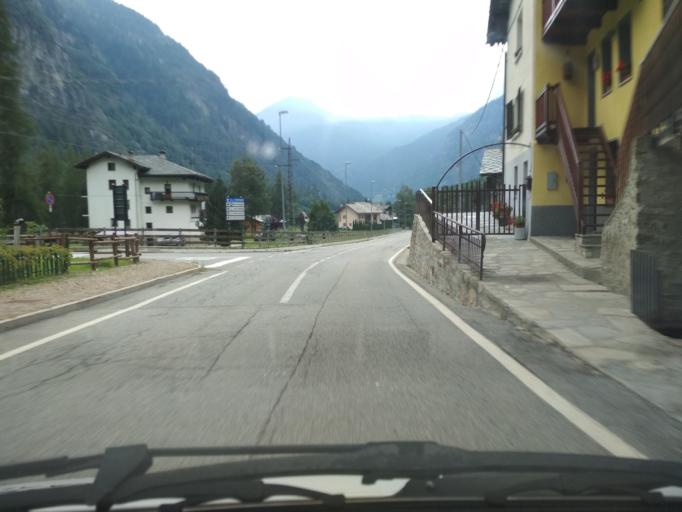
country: IT
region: Aosta Valley
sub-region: Valle d'Aosta
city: Gaby
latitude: 45.7050
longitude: 7.8772
